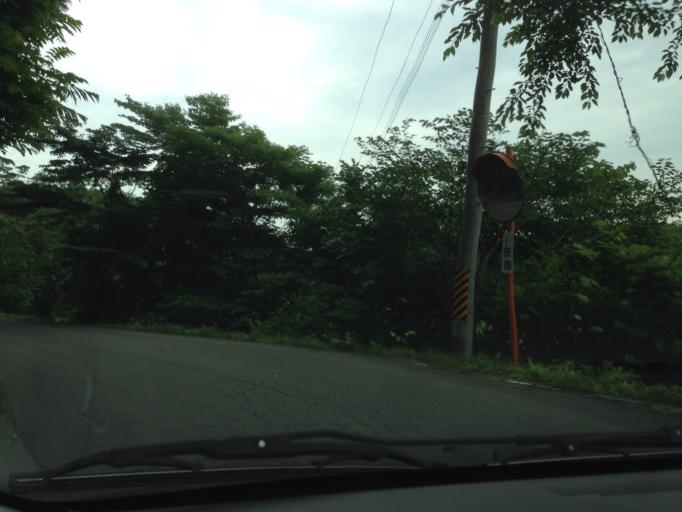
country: JP
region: Fukushima
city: Inawashiro
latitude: 37.5210
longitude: 140.0429
